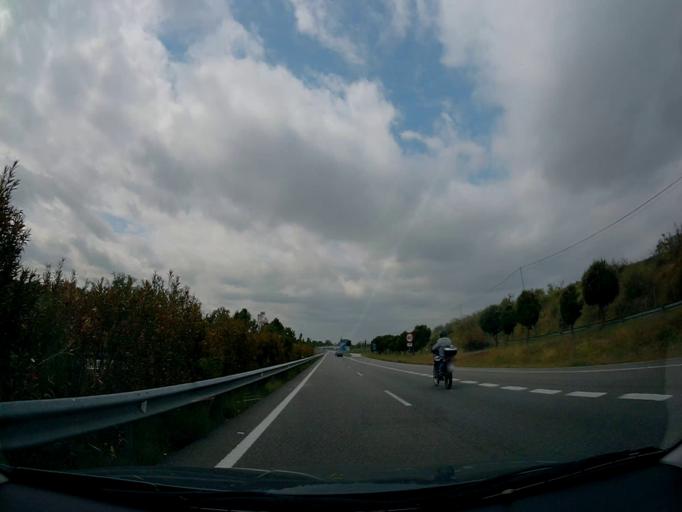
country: ES
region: Madrid
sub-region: Provincia de Madrid
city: Villaviciosa de Odon
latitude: 40.3845
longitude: -3.9044
